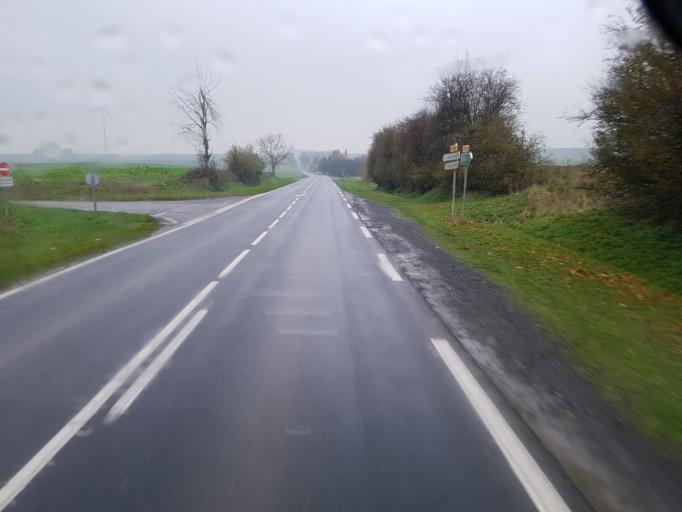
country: FR
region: Picardie
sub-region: Departement de l'Aisne
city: Saint-Quentin
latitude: 49.8887
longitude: 3.2657
